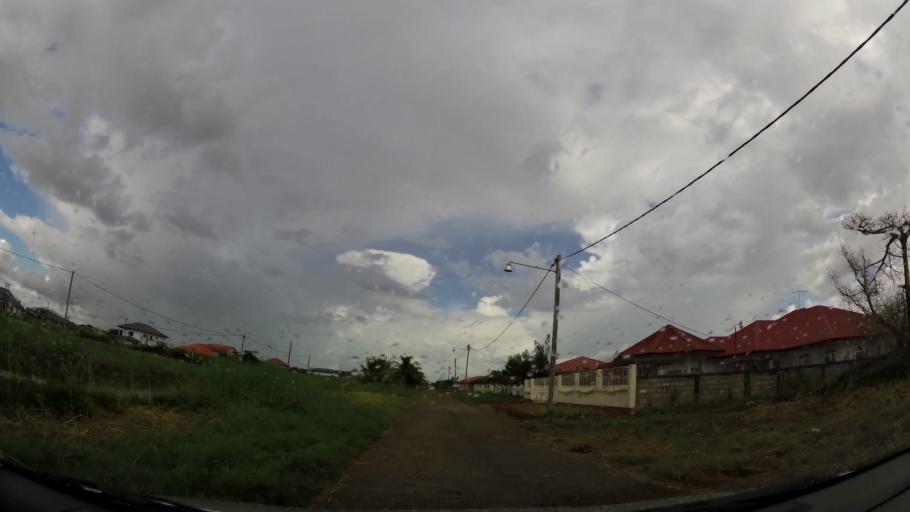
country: SR
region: Commewijne
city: Nieuw Amsterdam
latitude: 5.8641
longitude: -55.1169
